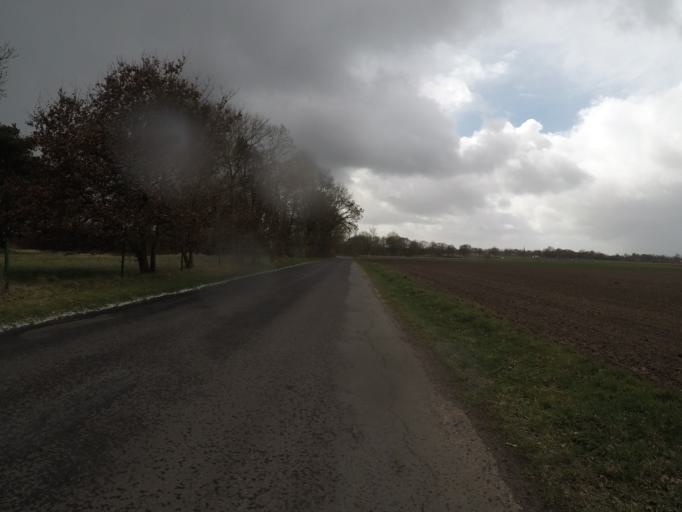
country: DE
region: Lower Saxony
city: Langen
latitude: 53.6244
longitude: 8.6571
